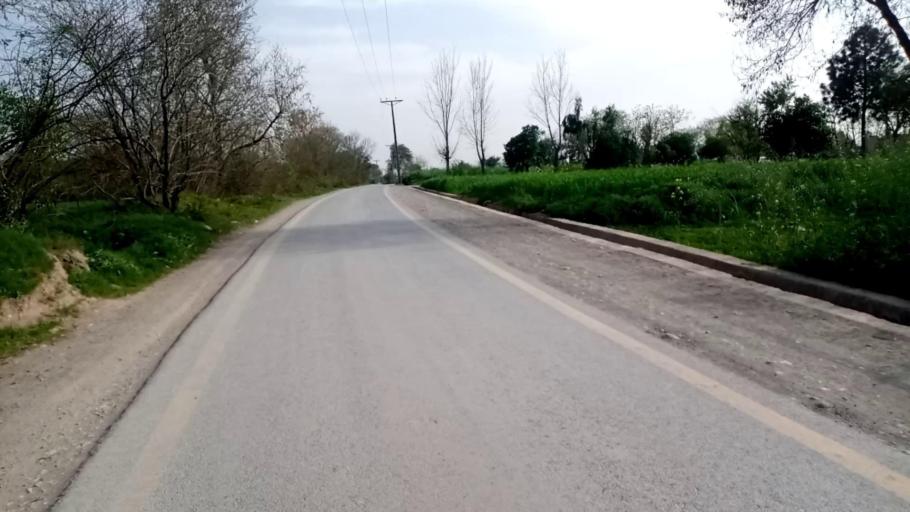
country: PK
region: Khyber Pakhtunkhwa
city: Peshawar
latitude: 34.0211
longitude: 71.4447
